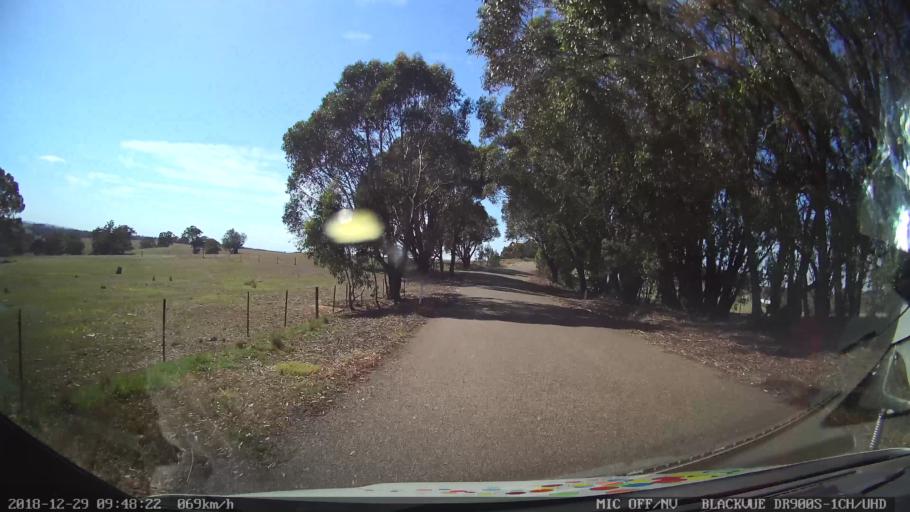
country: AU
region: New South Wales
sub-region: Upper Lachlan Shire
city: Crookwell
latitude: -34.7153
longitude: 149.4551
